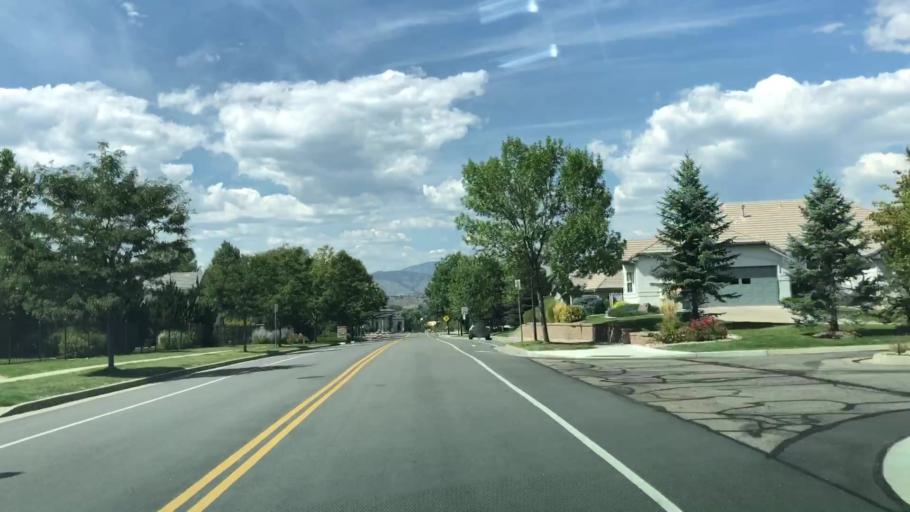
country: US
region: Colorado
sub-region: Larimer County
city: Loveland
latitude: 40.3971
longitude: -105.1464
